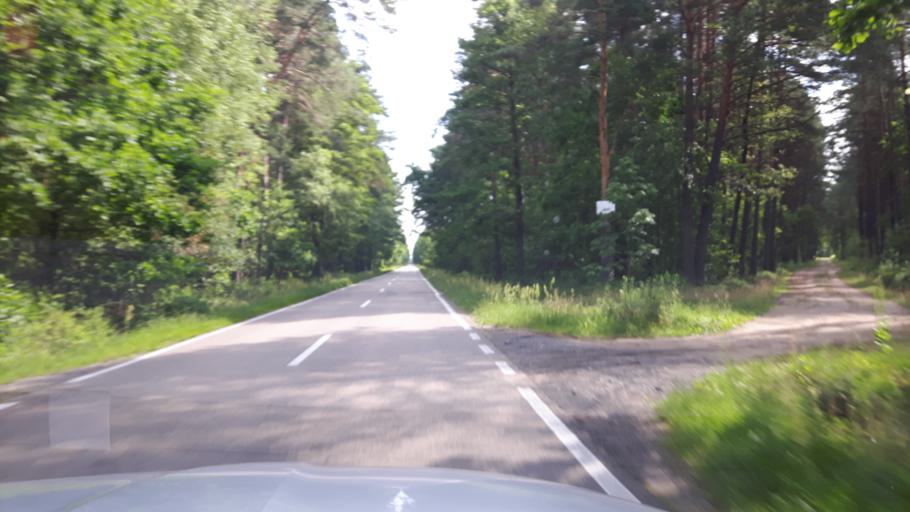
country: PL
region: Masovian Voivodeship
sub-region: Powiat wolominski
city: Tluszcz
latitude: 52.4284
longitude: 21.5344
